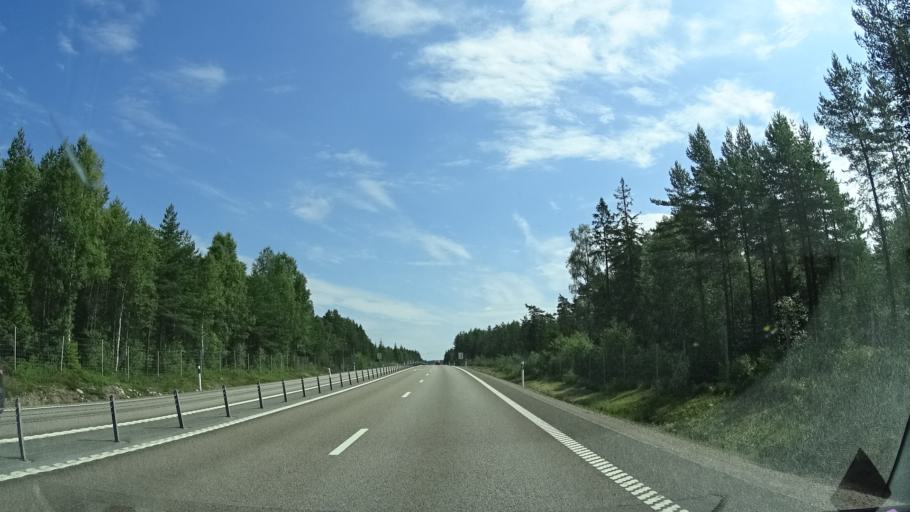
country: SE
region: Vaermland
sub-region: Kristinehamns Kommun
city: Bjorneborg
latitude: 59.3120
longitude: 14.2325
